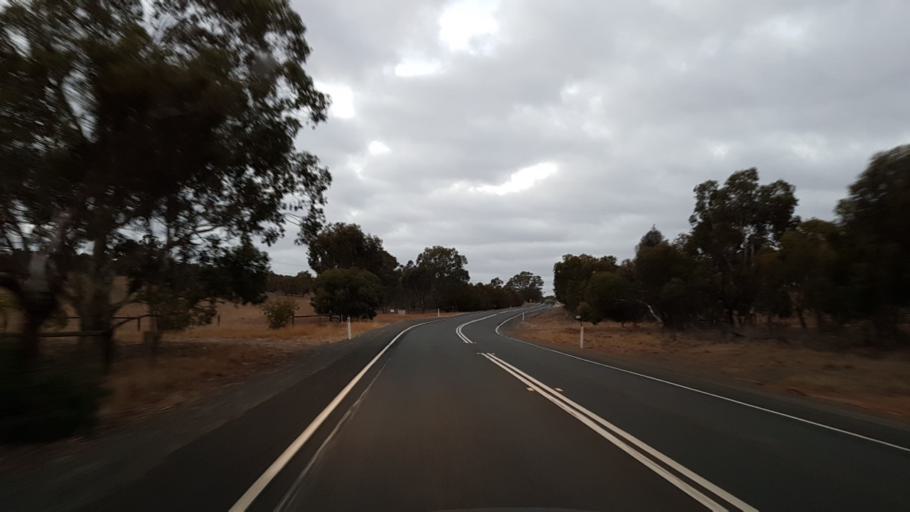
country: AU
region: South Australia
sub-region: Mount Barker
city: Nairne
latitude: -35.0445
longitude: 138.9958
